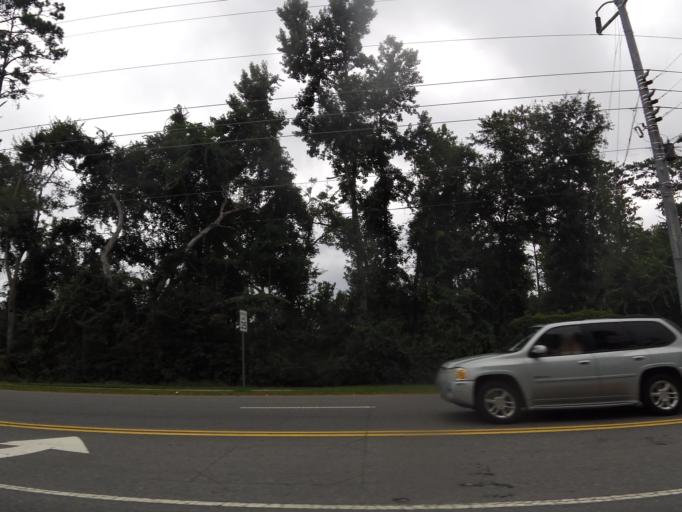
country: US
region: Georgia
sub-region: Glynn County
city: Saint Simon Mills
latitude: 31.1656
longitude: -81.4038
